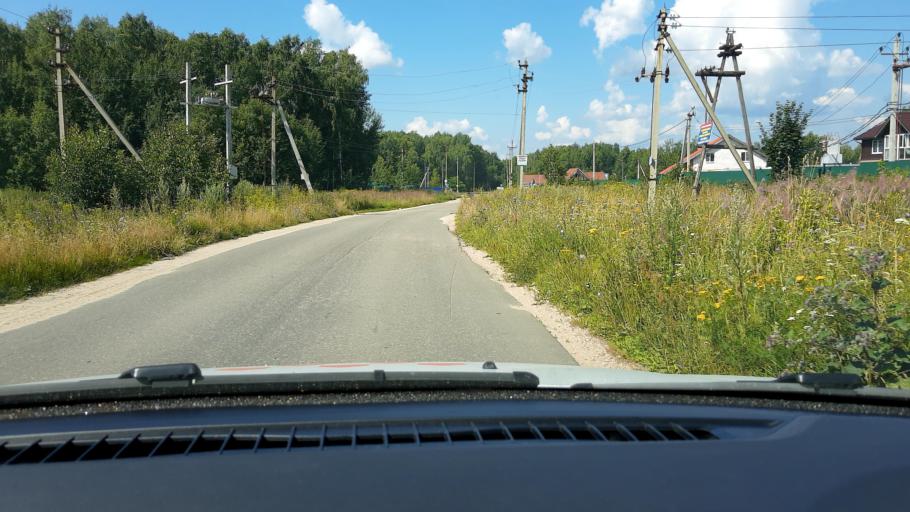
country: RU
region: Nizjnij Novgorod
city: Burevestnik
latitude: 56.0514
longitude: 43.9554
